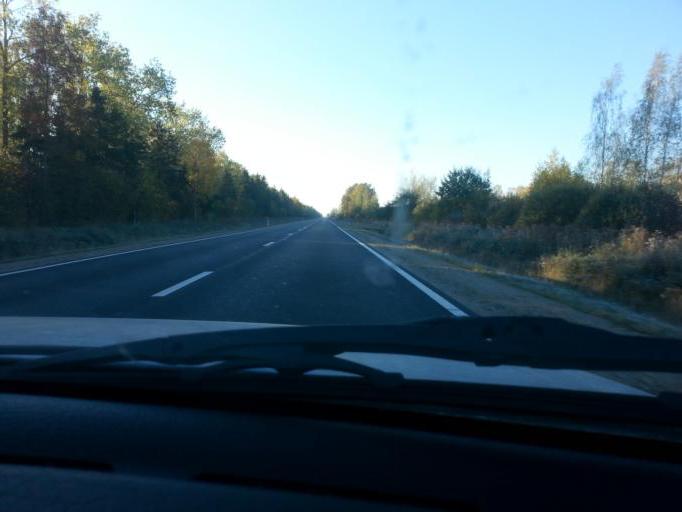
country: LV
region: Jelgava
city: Jelgava
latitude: 56.5001
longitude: 23.6998
